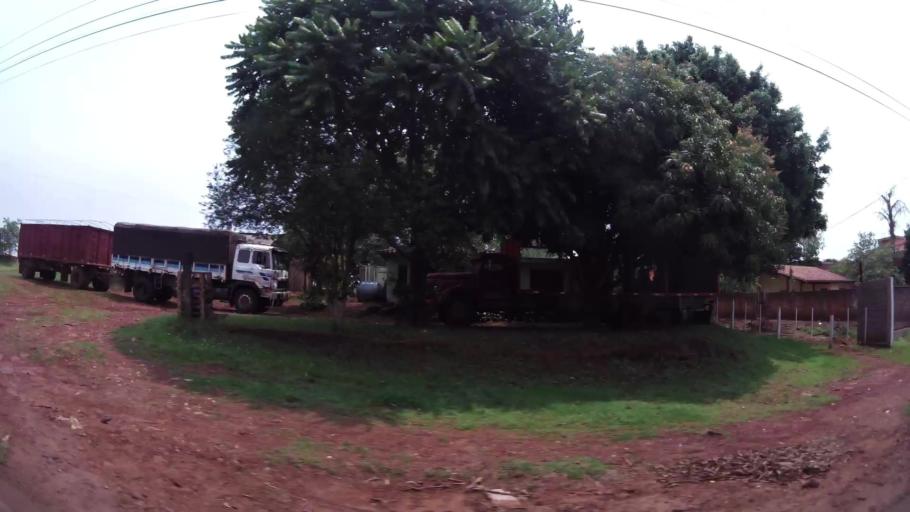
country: BR
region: Parana
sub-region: Foz Do Iguacu
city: Foz do Iguacu
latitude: -25.5753
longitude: -54.6030
